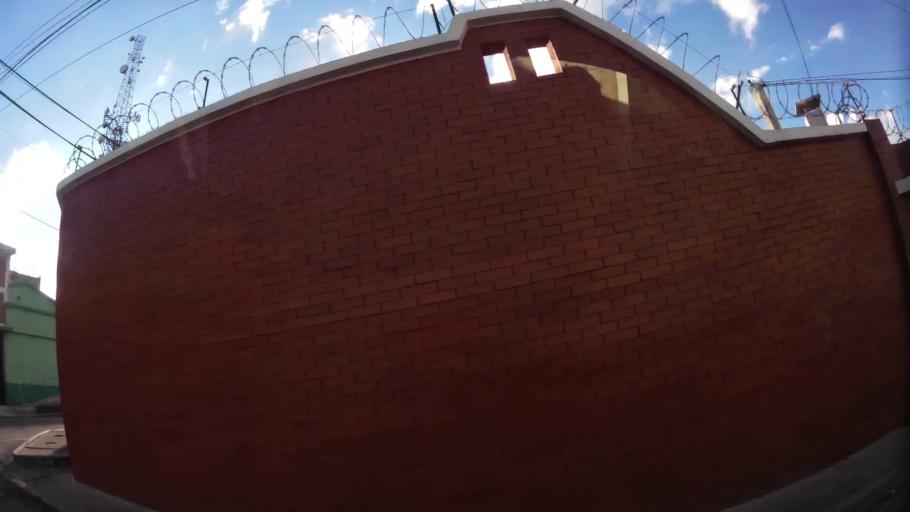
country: GT
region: Quetzaltenango
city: Quetzaltenango
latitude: 14.8520
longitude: -91.5252
